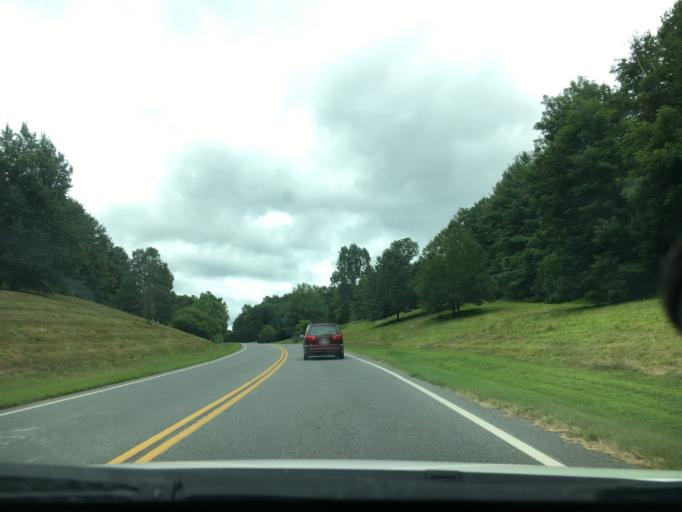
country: US
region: Virginia
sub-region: City of Charlottesville
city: Charlottesville
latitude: 38.0034
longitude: -78.4754
